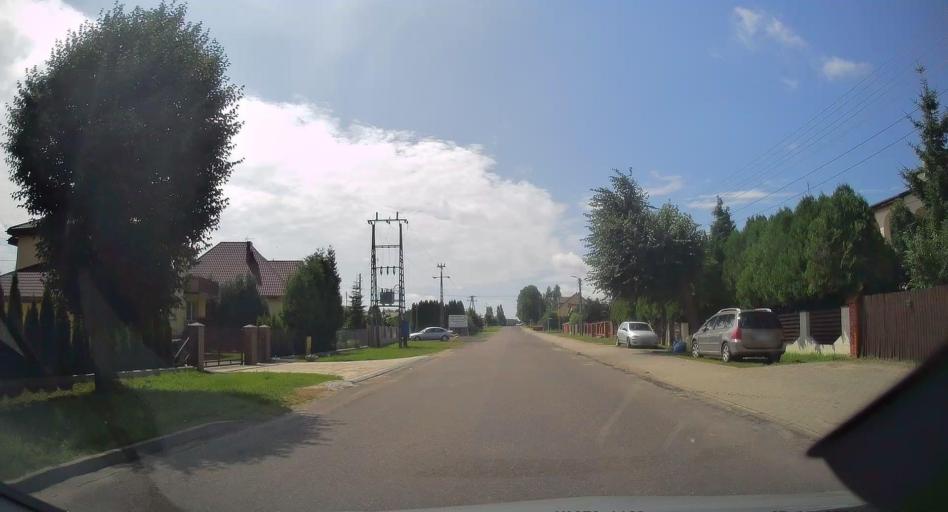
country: PL
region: Lodz Voivodeship
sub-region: Powiat rawski
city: Rawa Mazowiecka
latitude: 51.7483
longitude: 20.2390
